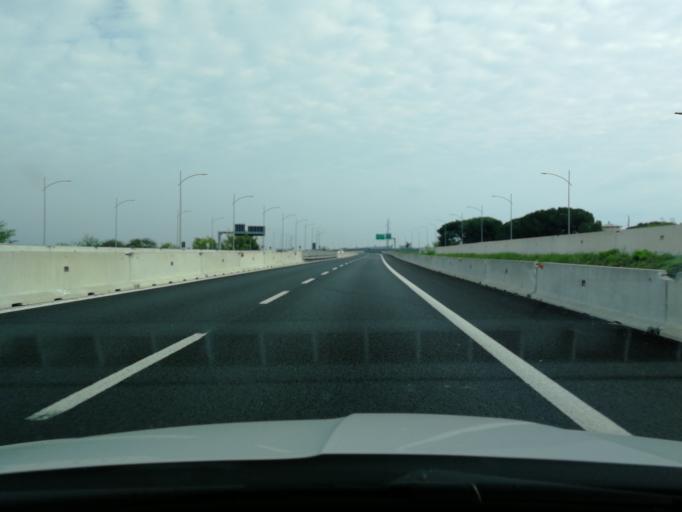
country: IT
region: Latium
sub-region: Citta metropolitana di Roma Capitale
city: Setteville
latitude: 41.9215
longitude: 12.6519
